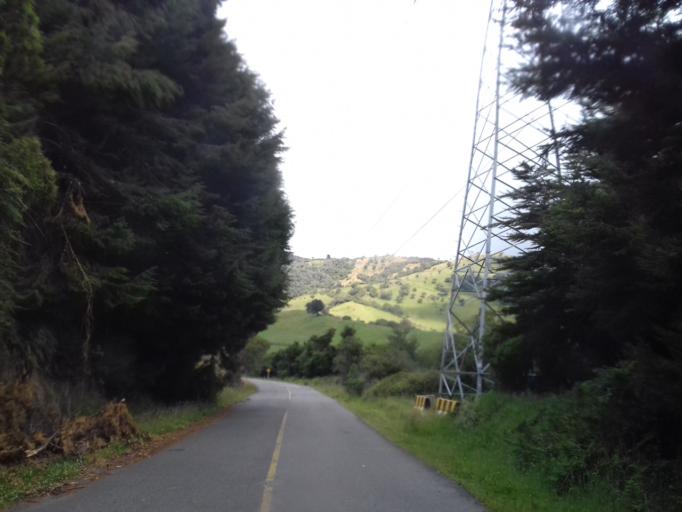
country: CO
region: Tolima
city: Herveo
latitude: 5.0157
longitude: -75.3344
